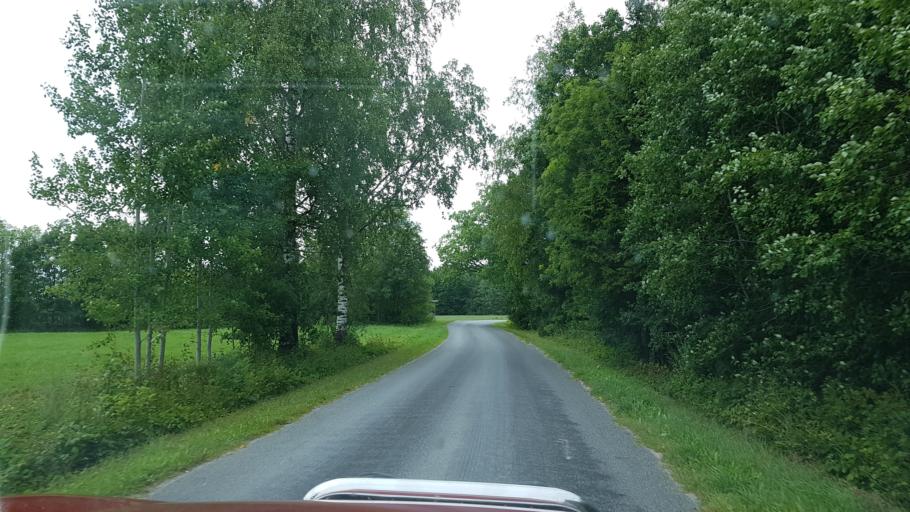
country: EE
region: Laeaene
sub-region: Ridala Parish
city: Uuemoisa
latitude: 59.0167
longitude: 23.7204
